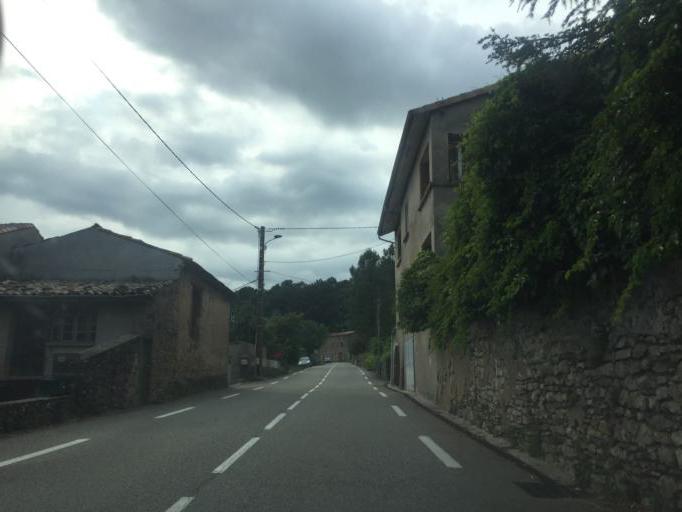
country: FR
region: Rhone-Alpes
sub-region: Departement de l'Ardeche
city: Privas
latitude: 44.7502
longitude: 4.5928
